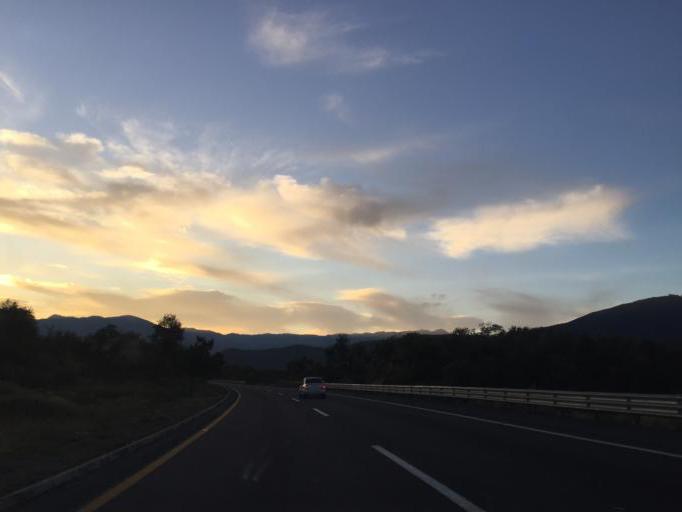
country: MX
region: Veracruz
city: Maltrata
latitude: 18.8355
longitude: -97.2612
